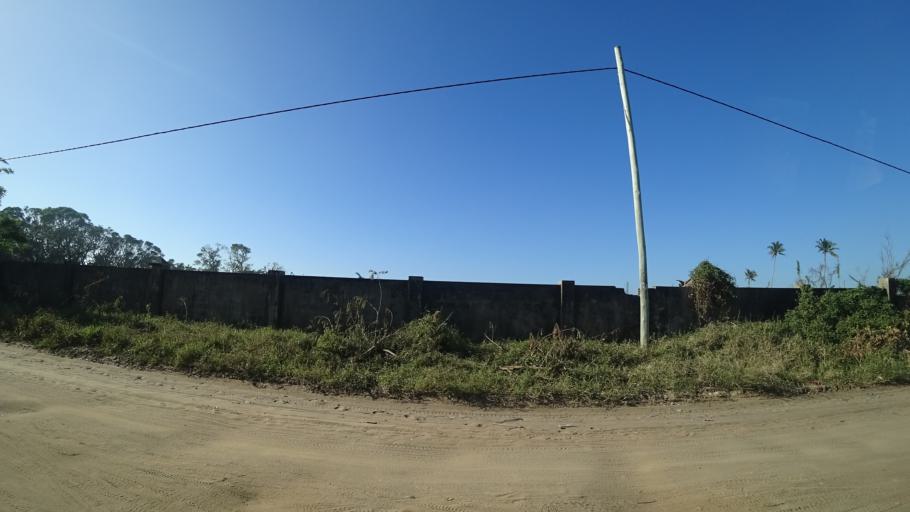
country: MZ
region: Sofala
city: Beira
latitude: -19.7682
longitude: 34.8917
